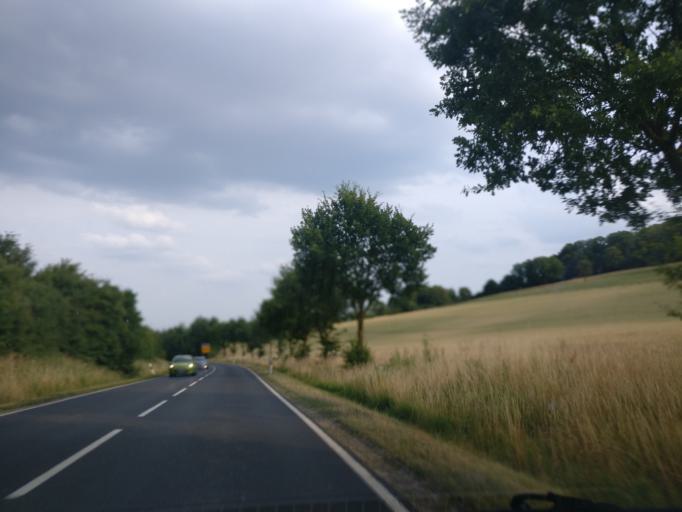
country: DE
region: Lower Saxony
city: Bovenden
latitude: 51.5805
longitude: 9.8696
